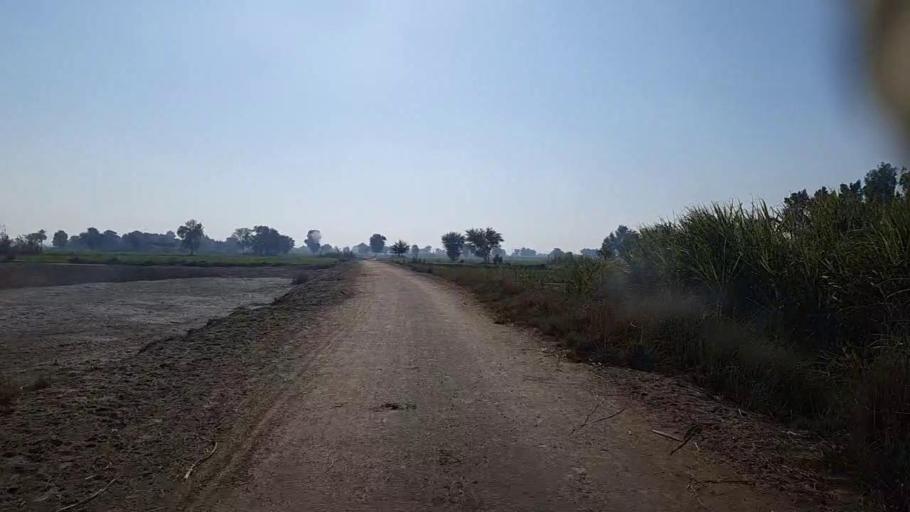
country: PK
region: Sindh
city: Khairpur
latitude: 28.0526
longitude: 69.7486
